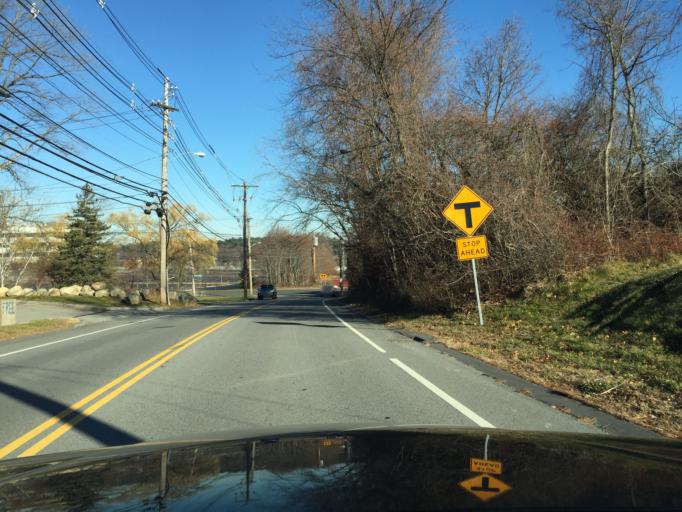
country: US
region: Massachusetts
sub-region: Middlesex County
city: Burlington
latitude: 42.4817
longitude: -71.1929
